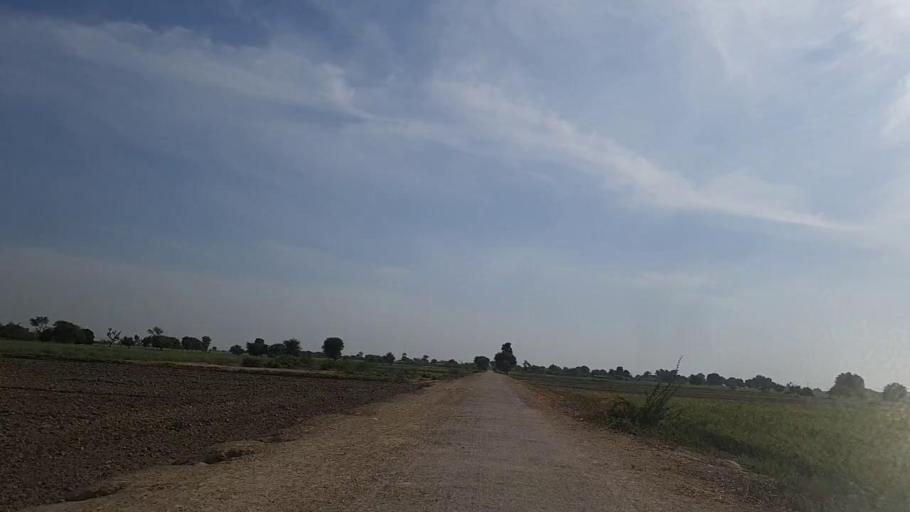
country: PK
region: Sindh
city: Samaro
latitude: 25.2284
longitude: 69.4323
